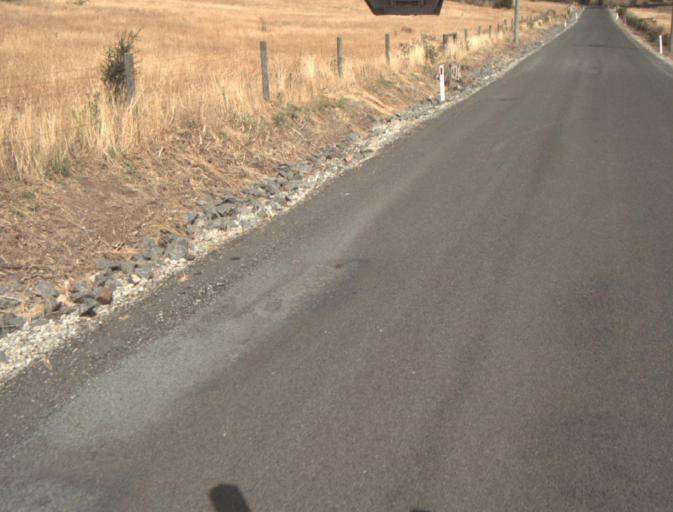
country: AU
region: Tasmania
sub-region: Launceston
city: Mayfield
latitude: -41.3102
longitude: 146.9954
